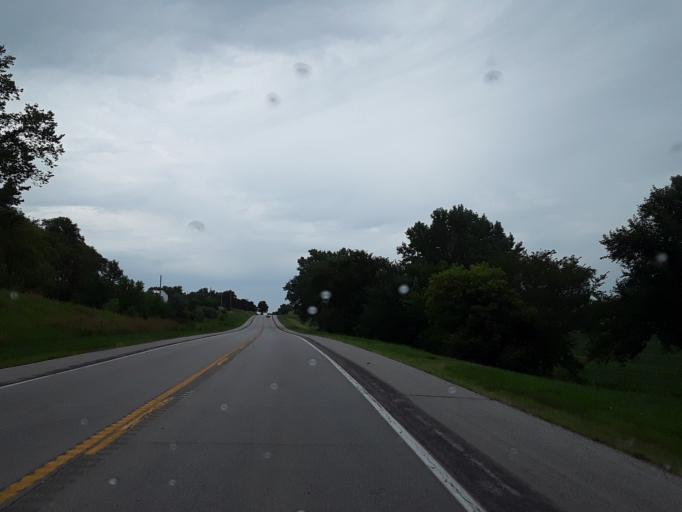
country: US
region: Nebraska
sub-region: Washington County
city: Blair
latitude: 41.5027
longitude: -96.1603
